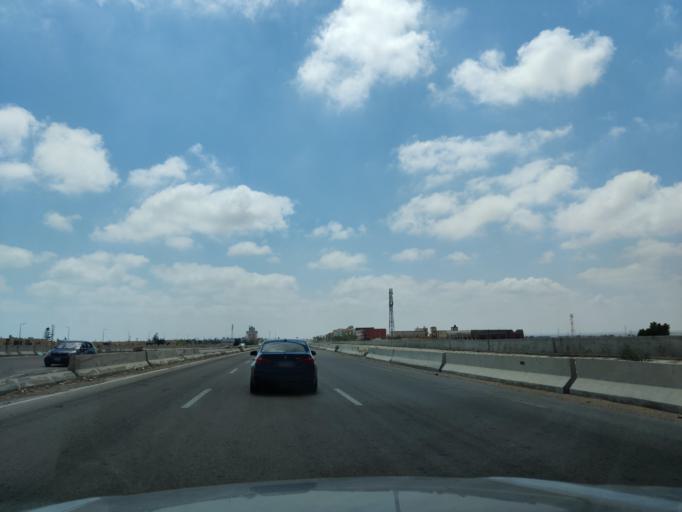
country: EG
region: Muhafazat Matruh
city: Al `Alamayn
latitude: 30.8208
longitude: 29.0171
